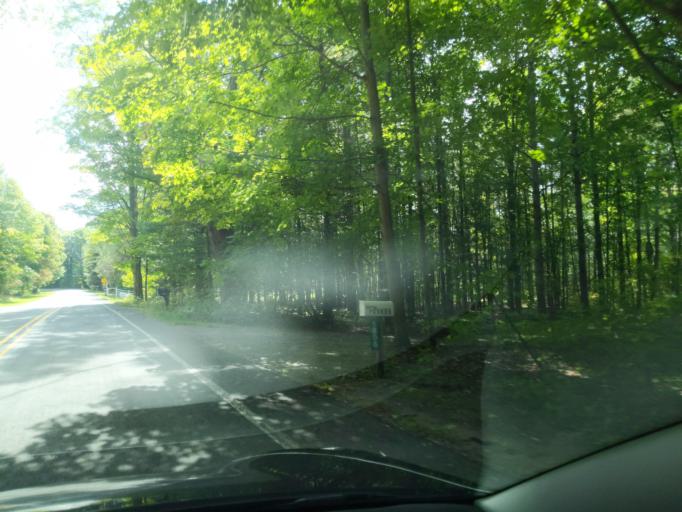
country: US
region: Michigan
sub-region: Antrim County
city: Bellaire
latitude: 45.0082
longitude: -85.2928
